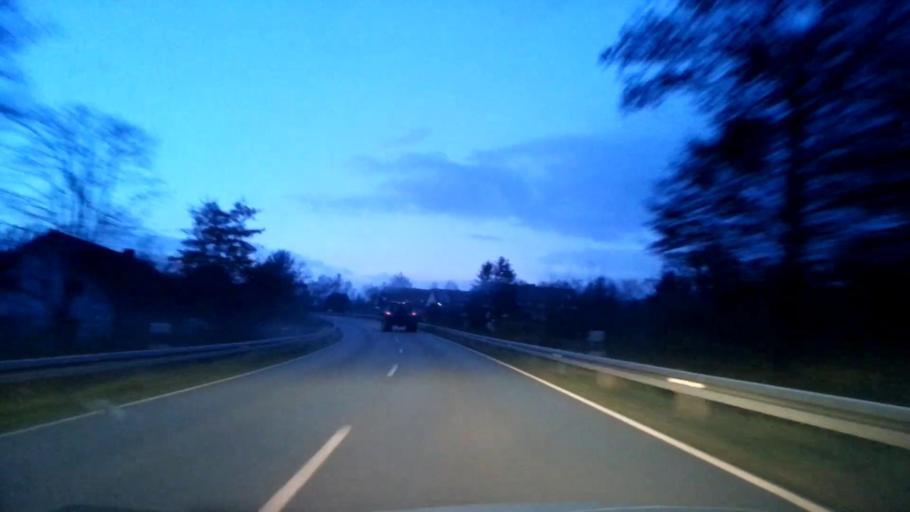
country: DE
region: Bavaria
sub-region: Upper Franconia
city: Reuth
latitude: 49.9573
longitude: 11.7044
